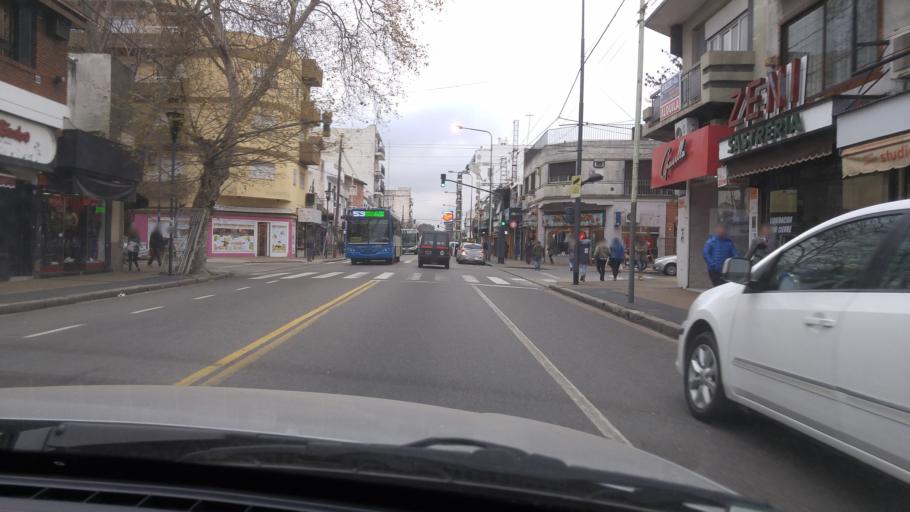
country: AR
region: Buenos Aires
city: Caseros
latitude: -34.6131
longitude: -58.5263
